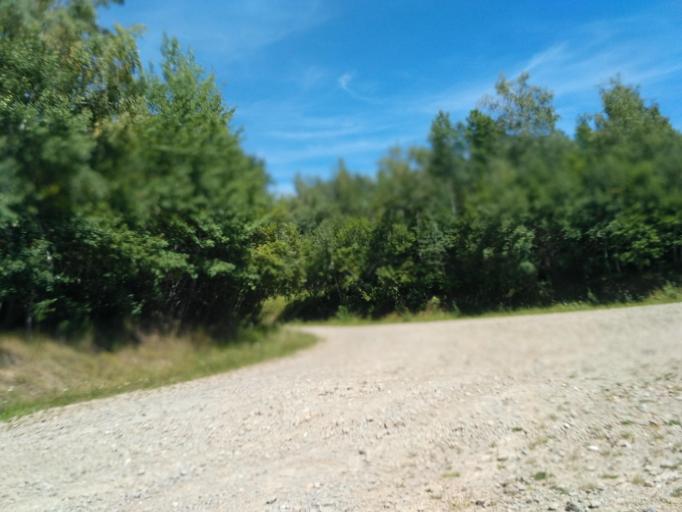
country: PL
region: Subcarpathian Voivodeship
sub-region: Powiat sanocki
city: Bukowsko
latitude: 49.4799
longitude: 22.0917
